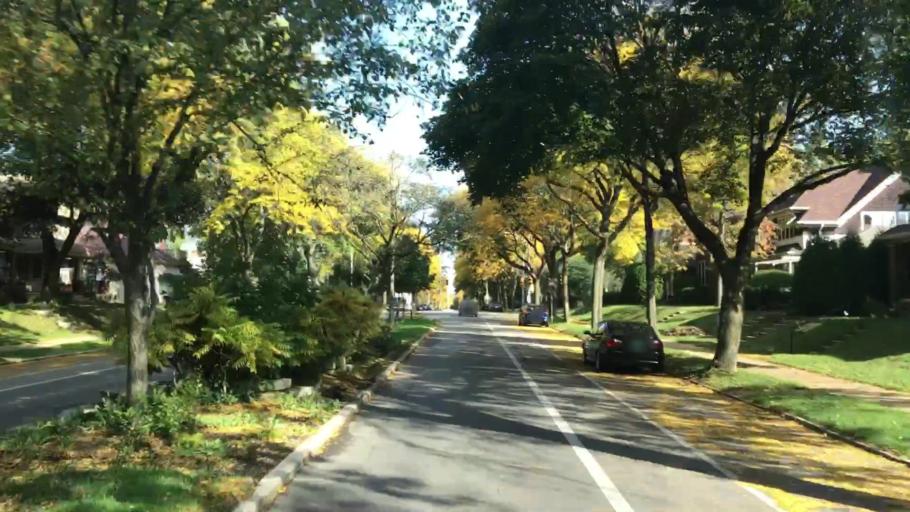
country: US
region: Wisconsin
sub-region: Milwaukee County
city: Shorewood
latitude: 43.0811
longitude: -87.8975
